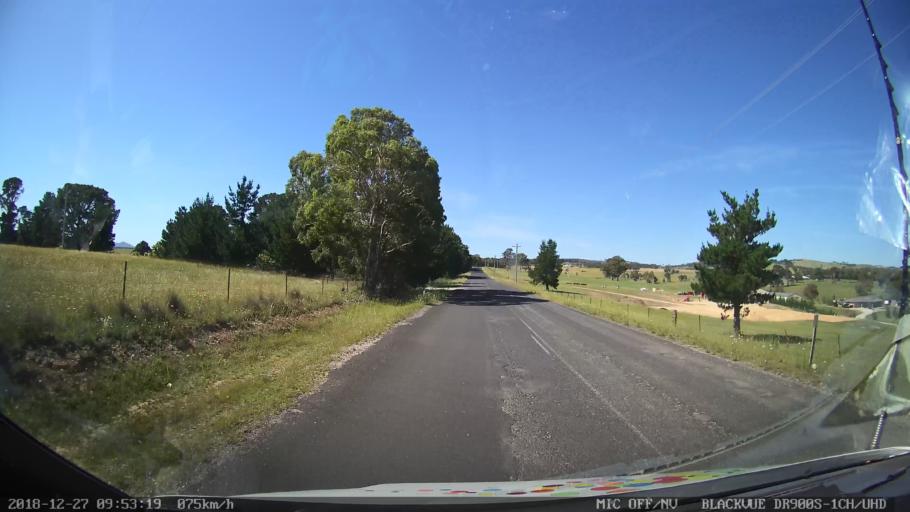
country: AU
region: New South Wales
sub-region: Lithgow
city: Portland
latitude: -33.3805
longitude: 149.9876
